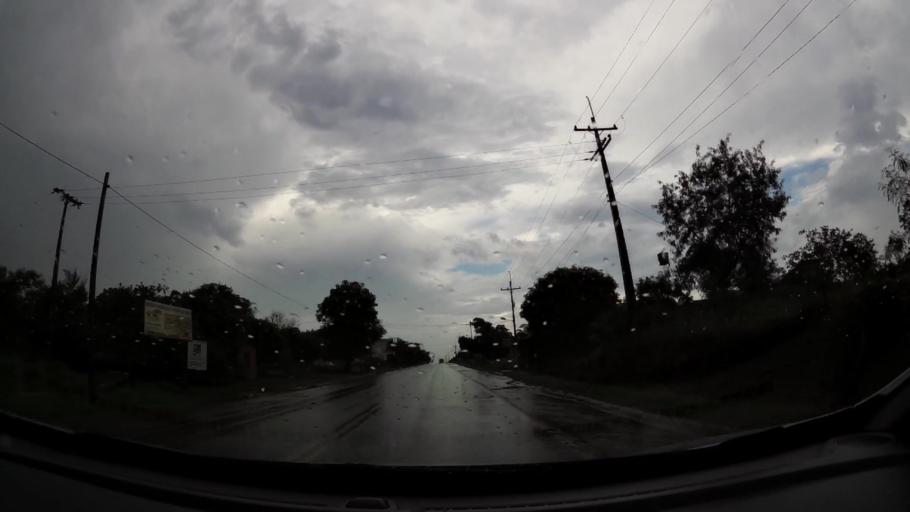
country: PY
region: Alto Parana
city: Presidente Franco
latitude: -25.5652
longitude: -54.6673
